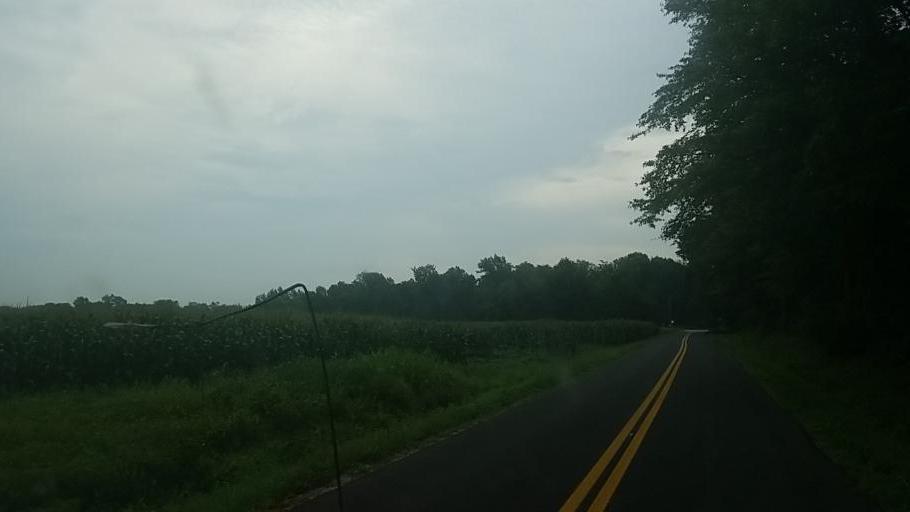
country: US
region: Delaware
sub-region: Sussex County
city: Selbyville
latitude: 38.4341
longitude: -75.2437
